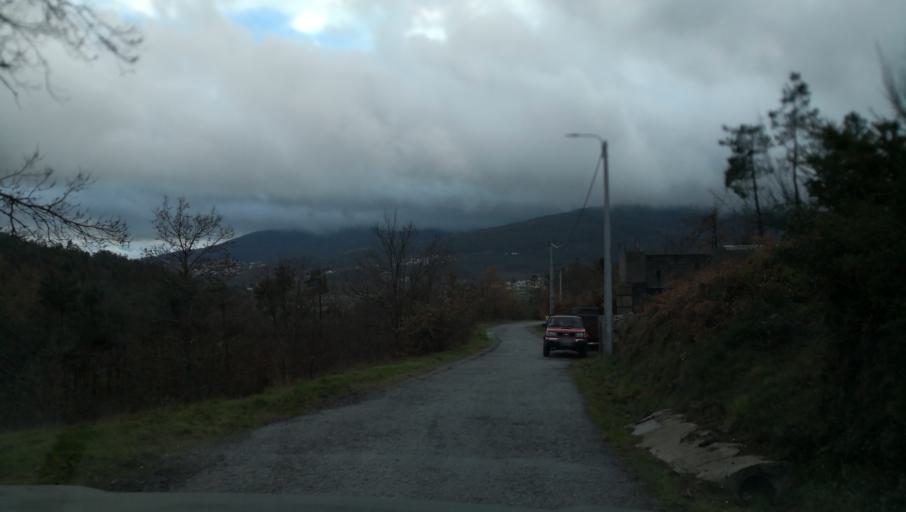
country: PT
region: Vila Real
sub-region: Santa Marta de Penaguiao
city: Santa Marta de Penaguiao
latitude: 41.3056
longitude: -7.8669
